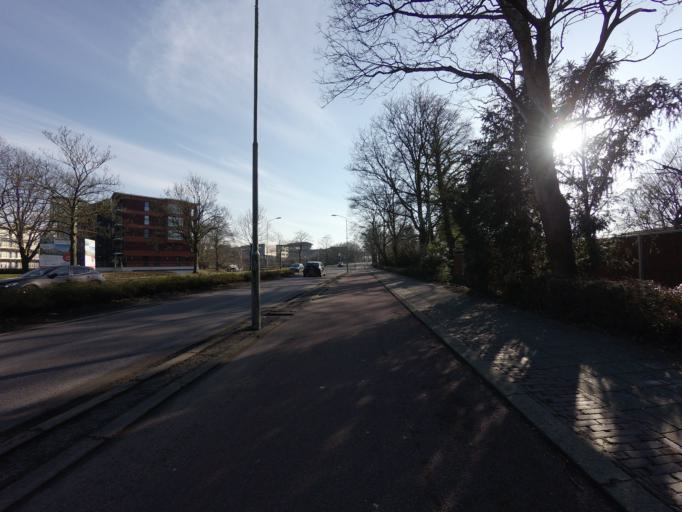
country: NL
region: South Holland
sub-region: Gemeente Gorinchem
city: Gorinchem
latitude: 51.8350
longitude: 4.9638
